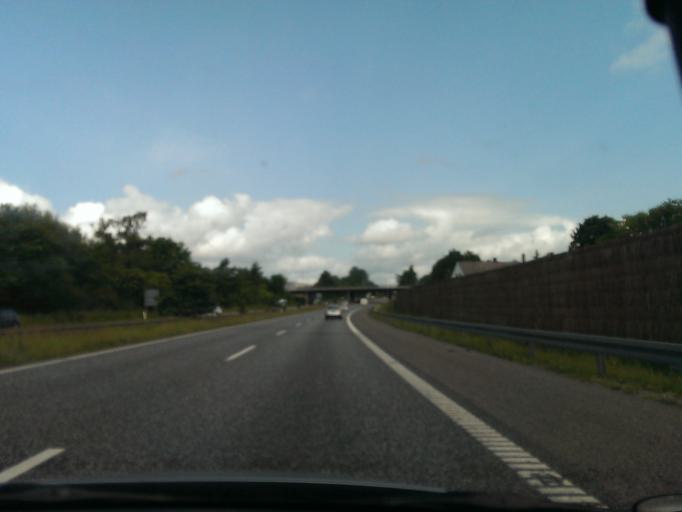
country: DK
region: Central Jutland
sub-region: Randers Kommune
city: Randers
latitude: 56.4598
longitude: 9.9881
